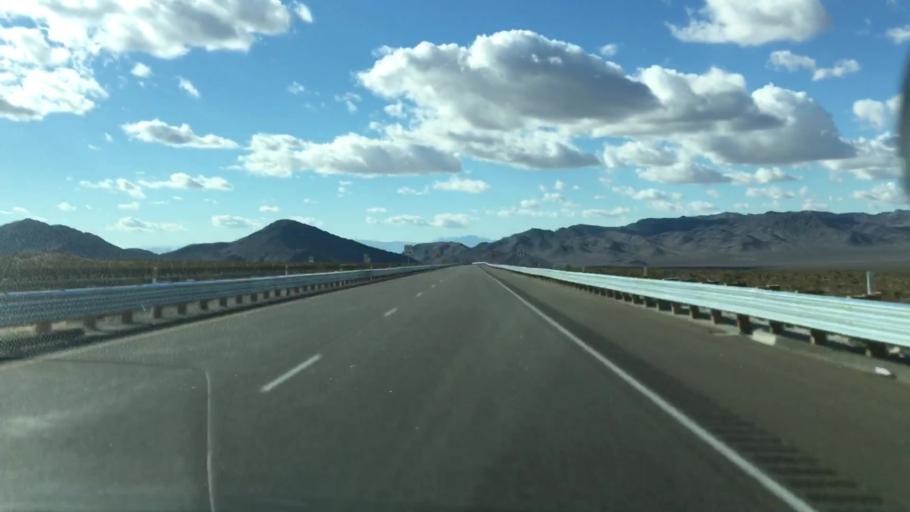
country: US
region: Nevada
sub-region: Nye County
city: Pahrump
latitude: 36.5971
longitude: -116.0041
